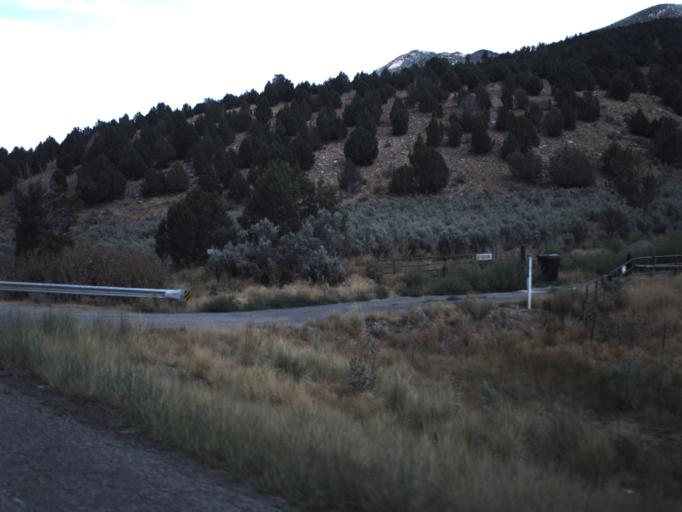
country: US
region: Utah
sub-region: Utah County
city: Woodland Hills
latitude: 39.8958
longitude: -111.5501
